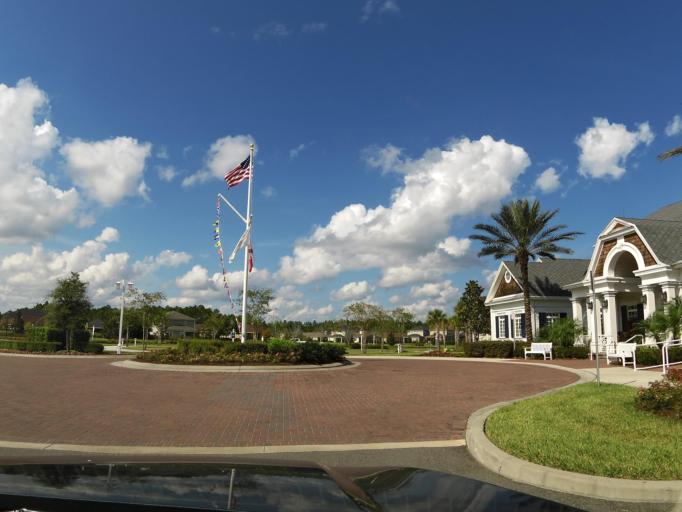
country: US
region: Florida
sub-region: Saint Johns County
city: Palm Valley
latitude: 30.0738
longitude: -81.4698
